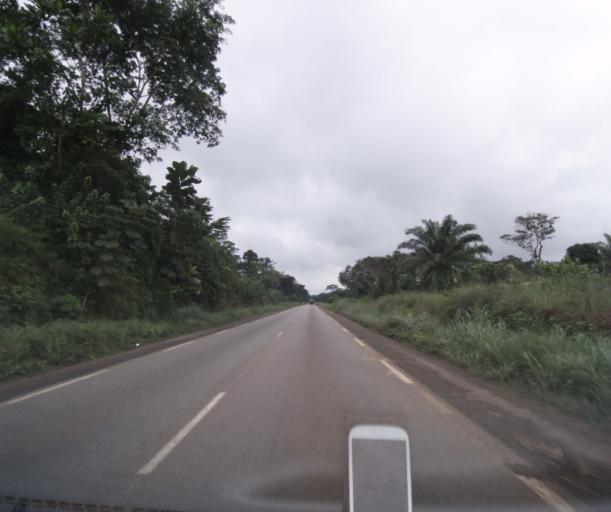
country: CM
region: Littoral
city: Edea
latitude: 3.8144
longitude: 10.3220
